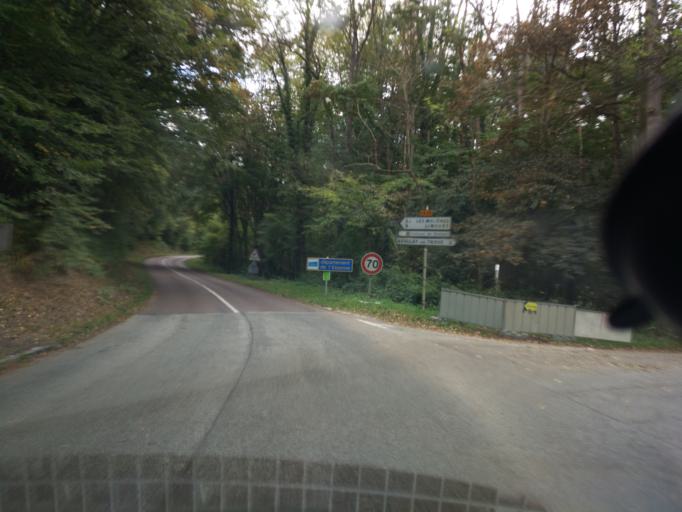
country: FR
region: Ile-de-France
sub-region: Departement de l'Essonne
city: Les Molieres
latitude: 48.6885
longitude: 2.0645
